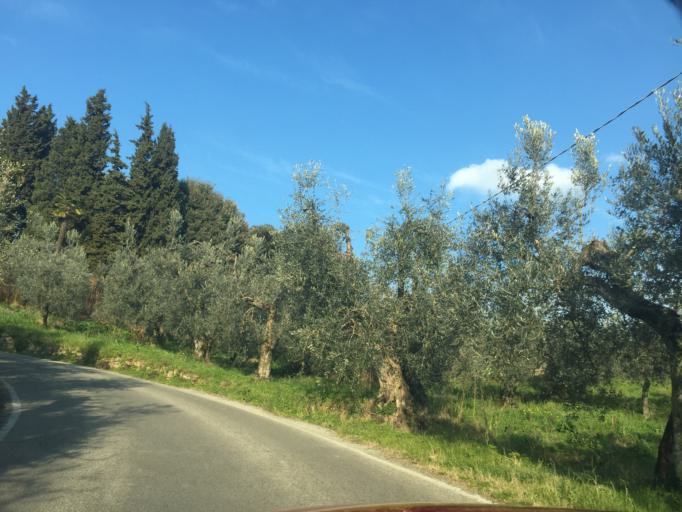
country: IT
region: Tuscany
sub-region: Province of Florence
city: Vinci
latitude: 43.7962
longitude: 10.9302
